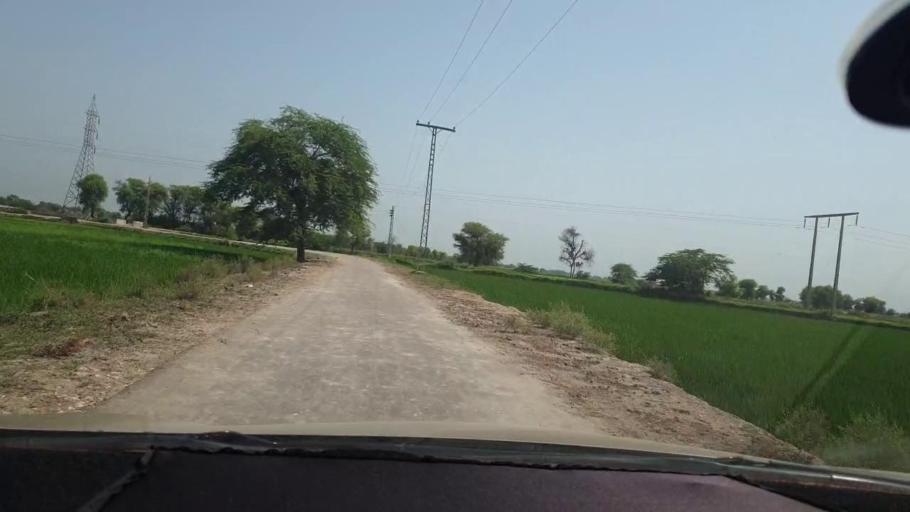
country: PK
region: Sindh
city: Goth Garelo
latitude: 27.4994
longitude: 68.0178
